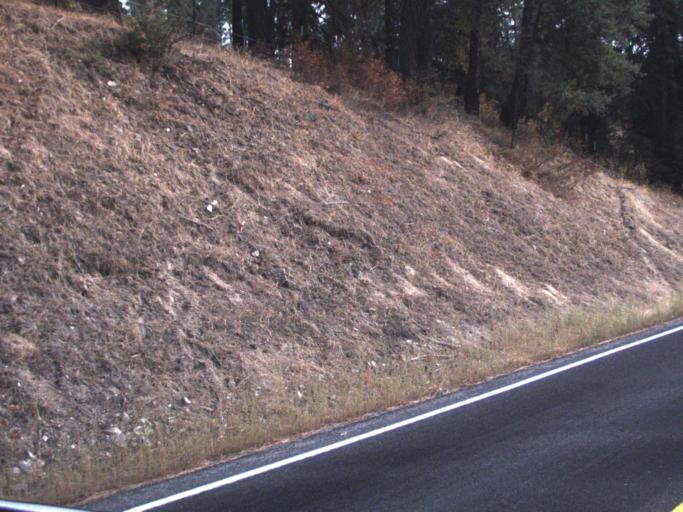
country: US
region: Washington
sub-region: Spokane County
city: Trentwood
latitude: 47.8317
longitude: -117.2002
